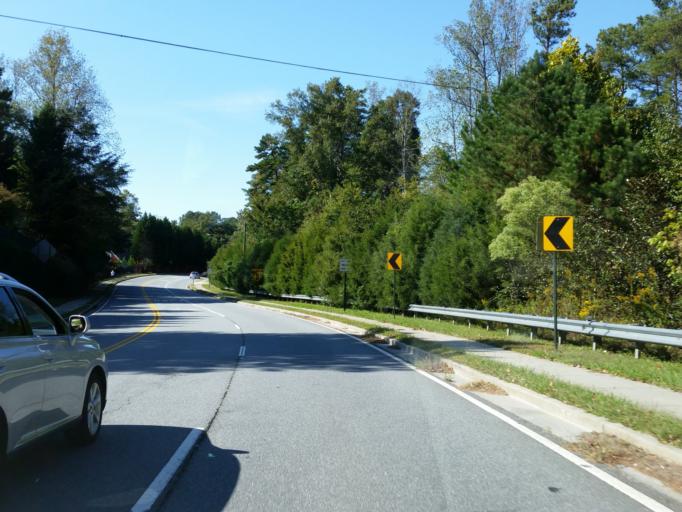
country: US
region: Georgia
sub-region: Cobb County
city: Smyrna
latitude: 33.9509
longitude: -84.4628
